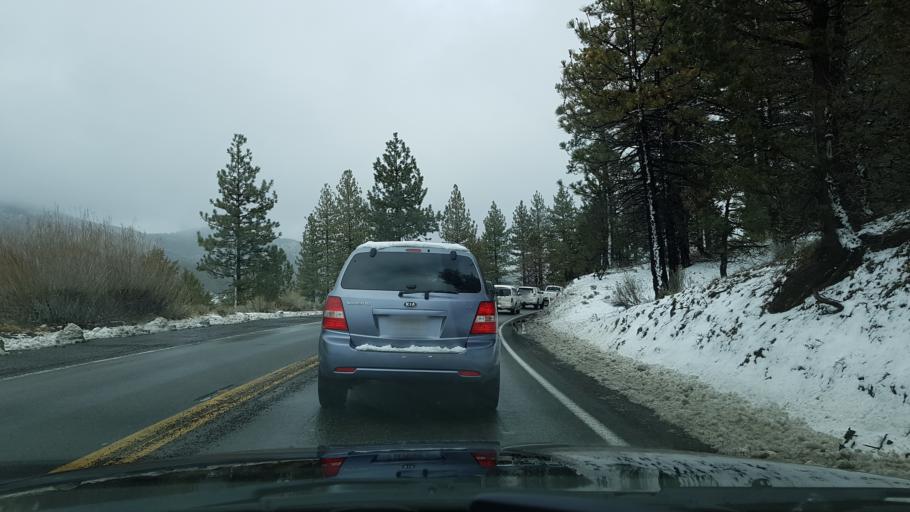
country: US
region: California
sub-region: San Bernardino County
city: Big Bear City
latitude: 34.2590
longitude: -116.8797
